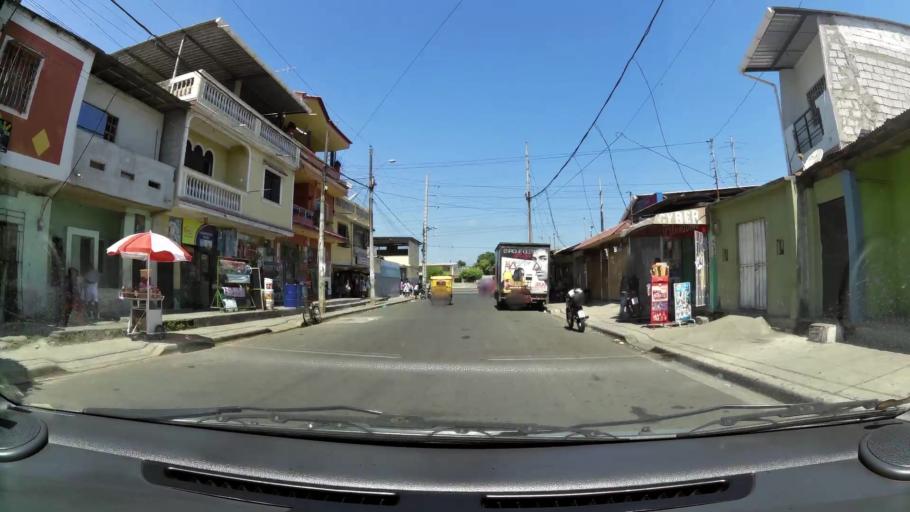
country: EC
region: Guayas
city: Guayaquil
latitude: -2.2392
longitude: -79.9182
